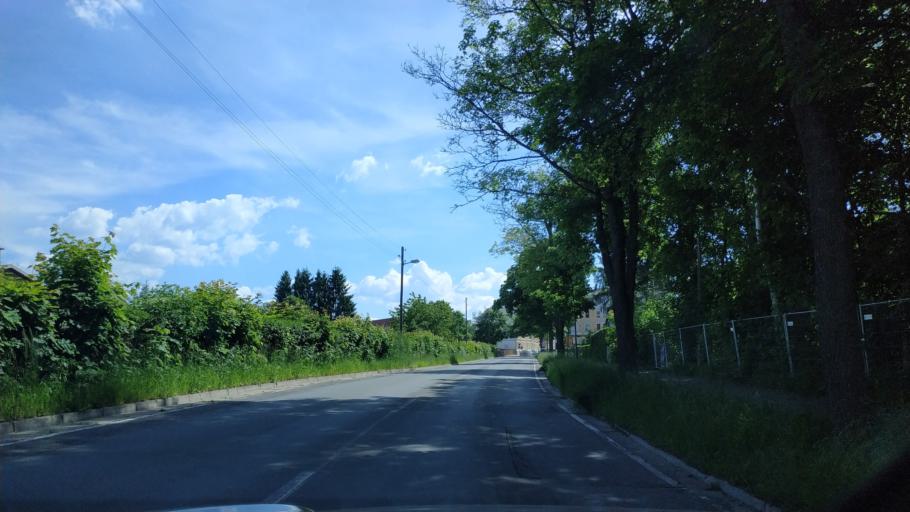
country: DE
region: Saxony
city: Plauen
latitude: 50.5168
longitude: 12.1325
